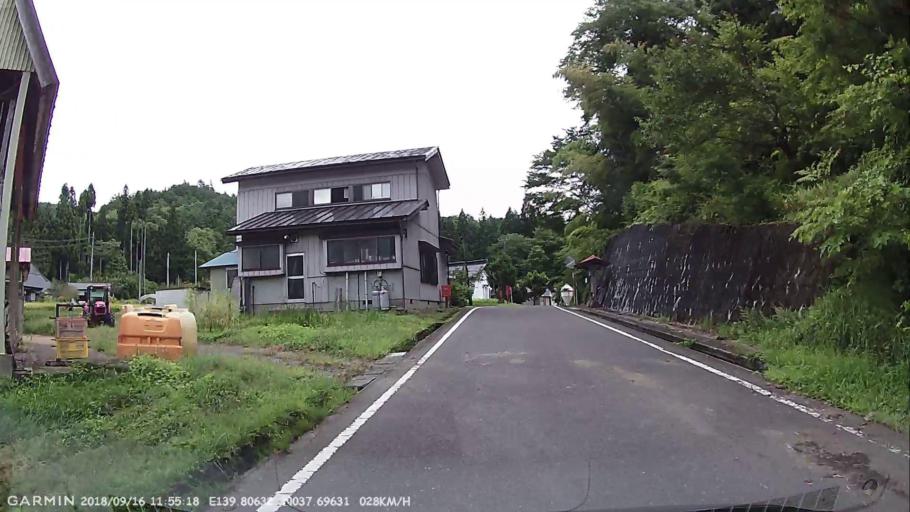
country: JP
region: Fukushima
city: Kitakata
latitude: 37.6963
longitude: 139.8063
